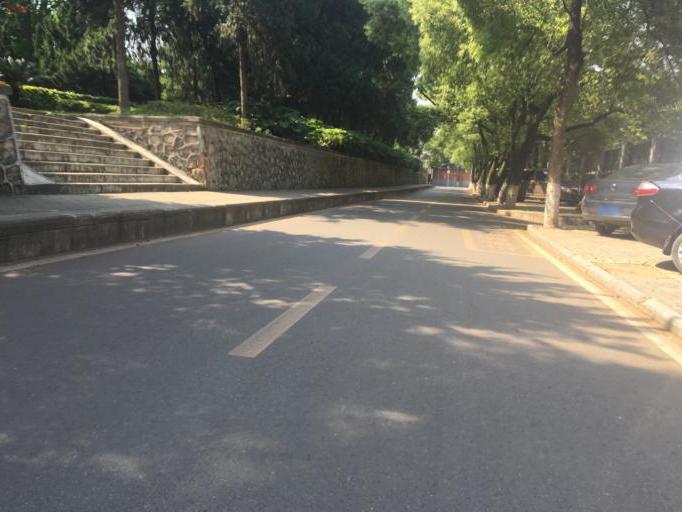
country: CN
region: Hubei
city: Guanshan
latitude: 30.5308
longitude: 114.3575
